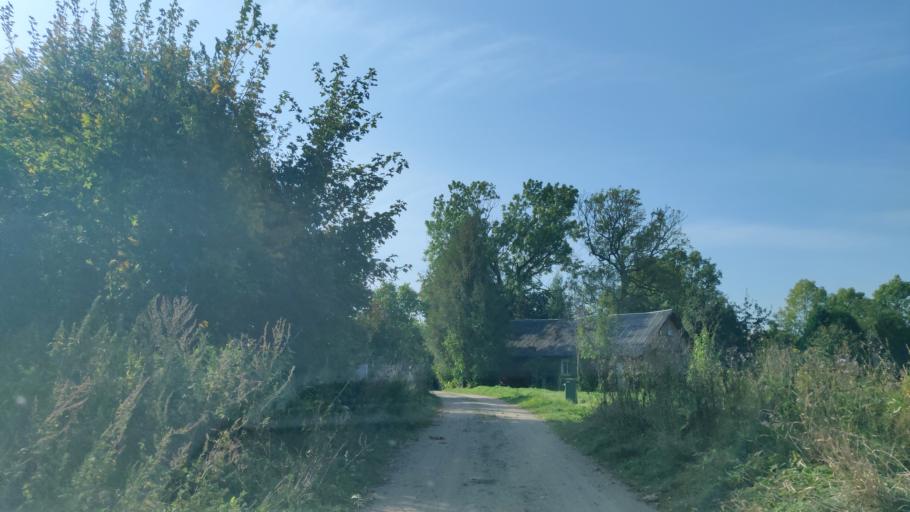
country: LT
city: Sirvintos
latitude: 54.9617
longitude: 24.7842
